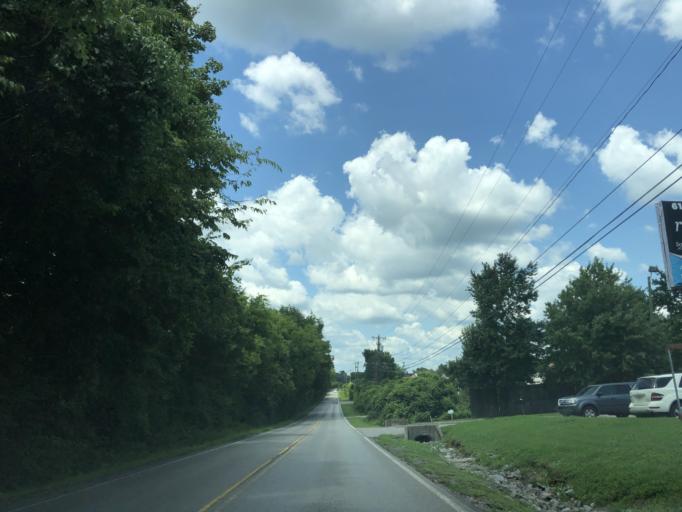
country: US
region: Tennessee
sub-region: Davidson County
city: Lakewood
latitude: 36.2170
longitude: -86.6047
